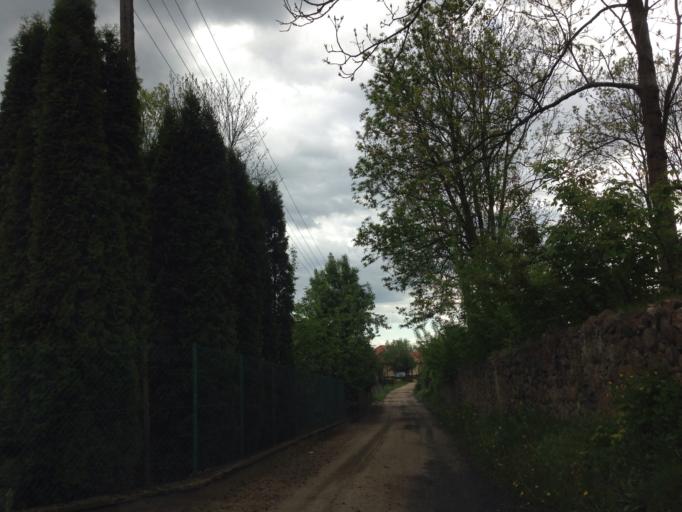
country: PL
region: Podlasie
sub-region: Powiat lomzynski
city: Wizna
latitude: 53.1887
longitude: 22.3841
